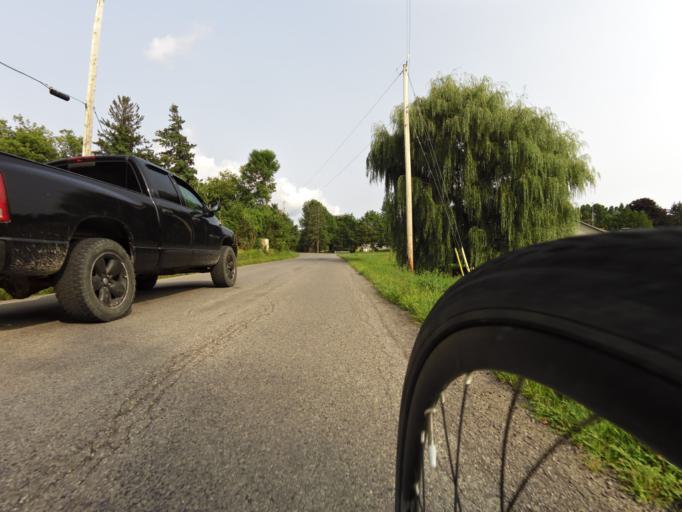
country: CA
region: Ontario
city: Quinte West
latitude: 44.0518
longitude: -77.6317
